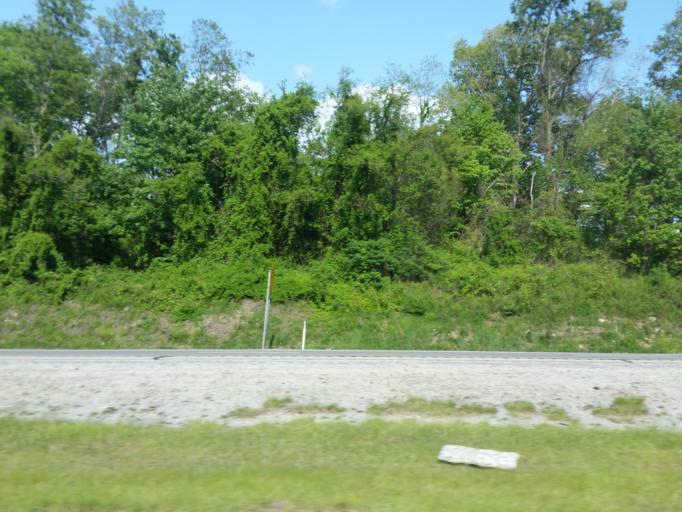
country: US
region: West Virginia
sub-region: Raleigh County
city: Mabscott
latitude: 37.7777
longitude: -81.2212
